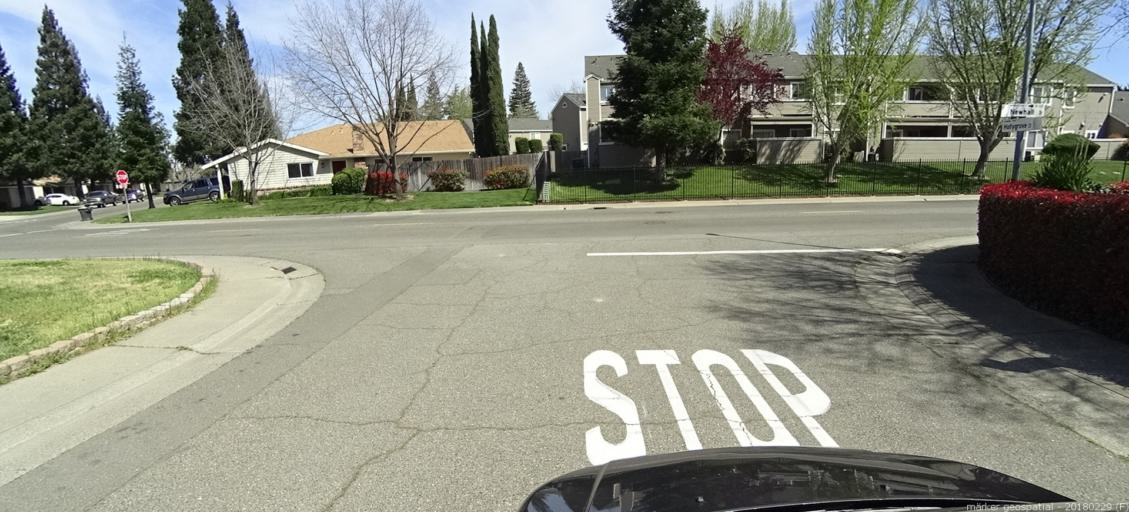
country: US
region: California
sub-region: Sacramento County
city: Rosemont
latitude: 38.5424
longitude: -121.3621
